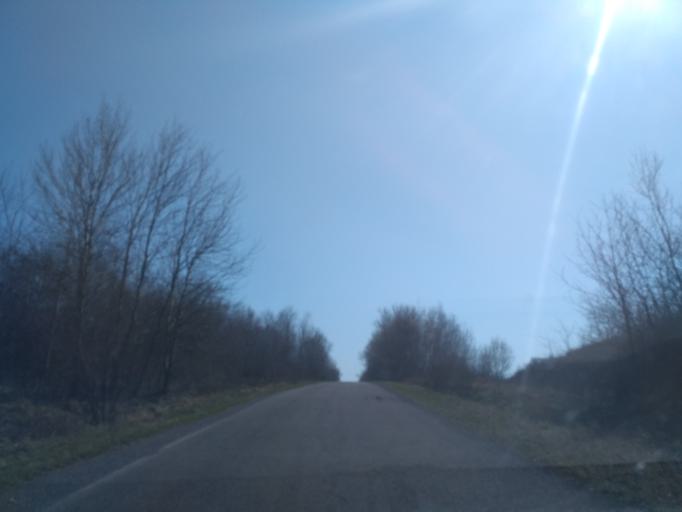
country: SK
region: Presovsky
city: Vranov nad Topl'ou
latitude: 48.8209
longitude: 21.6377
